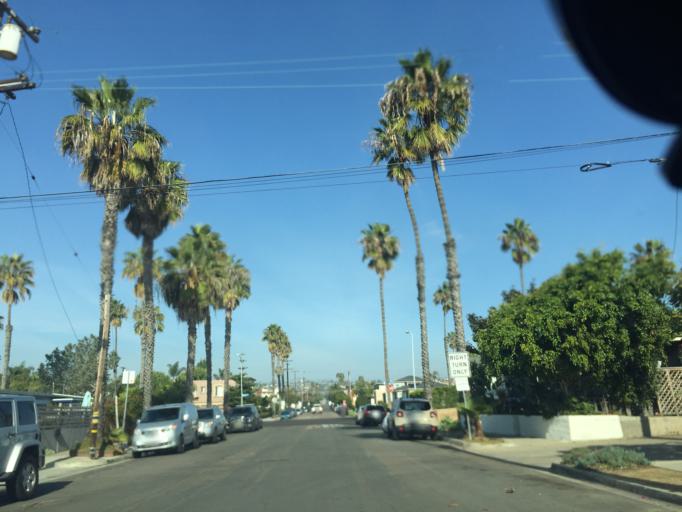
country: US
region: California
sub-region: San Diego County
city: La Jolla
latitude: 32.7956
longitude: -117.2474
